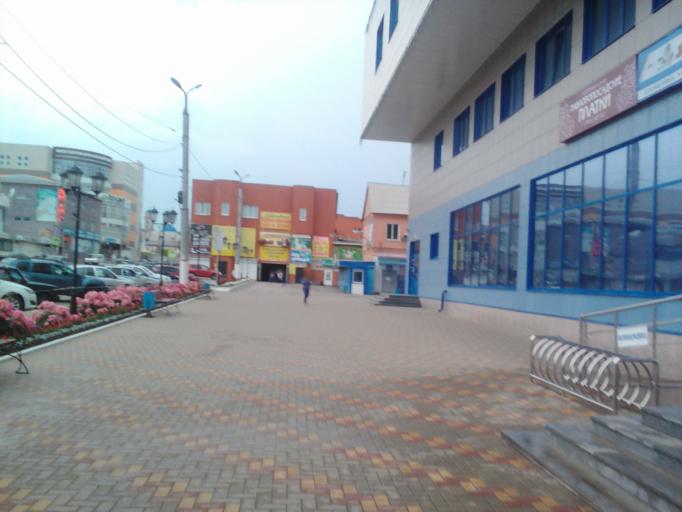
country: RU
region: Kursk
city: Kursk
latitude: 51.7292
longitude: 36.1828
